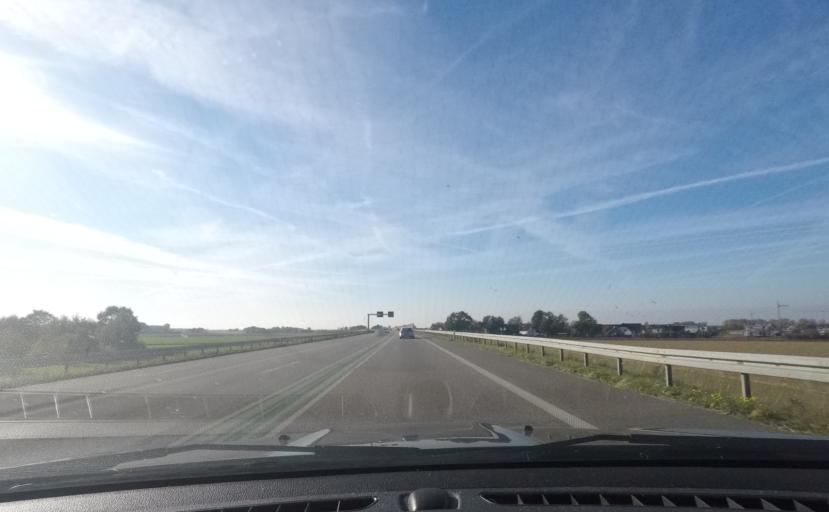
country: DE
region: North Rhine-Westphalia
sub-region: Regierungsbezirk Munster
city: Borken
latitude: 51.8298
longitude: 6.8454
